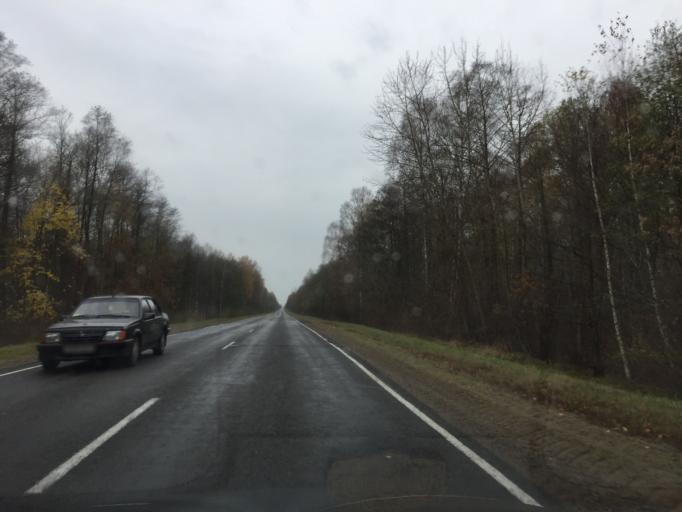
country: BY
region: Mogilev
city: Slawharad
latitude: 53.3655
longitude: 30.8518
